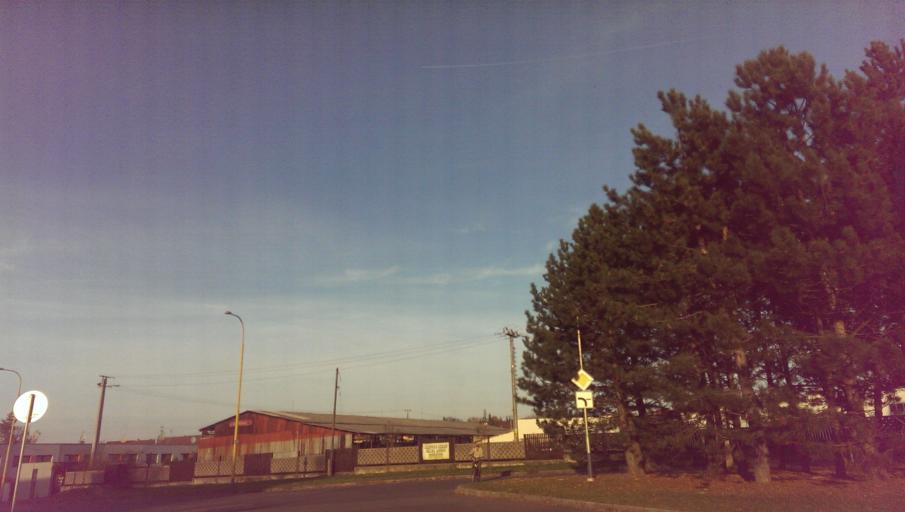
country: CZ
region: Zlin
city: Kunovice
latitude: 49.0594
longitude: 17.4843
